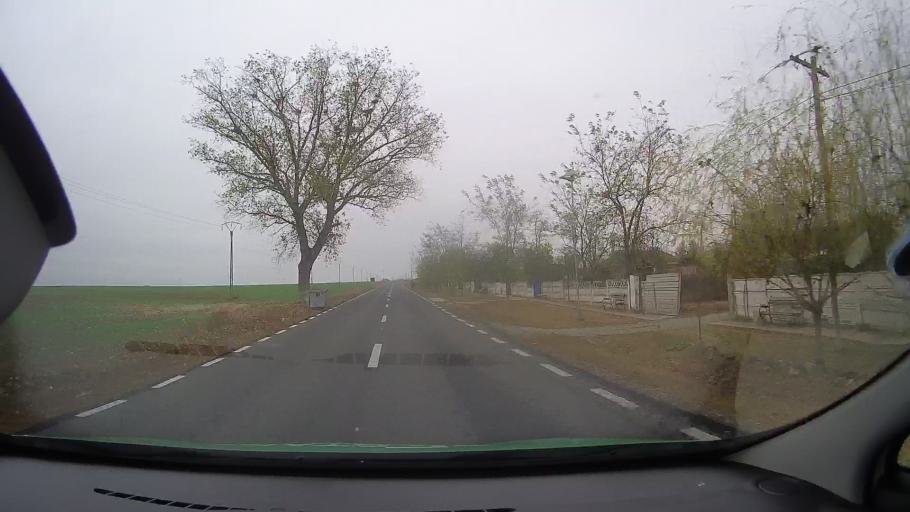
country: RO
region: Constanta
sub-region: Comuna Tortoman
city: Tortoman
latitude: 44.3502
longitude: 28.2172
